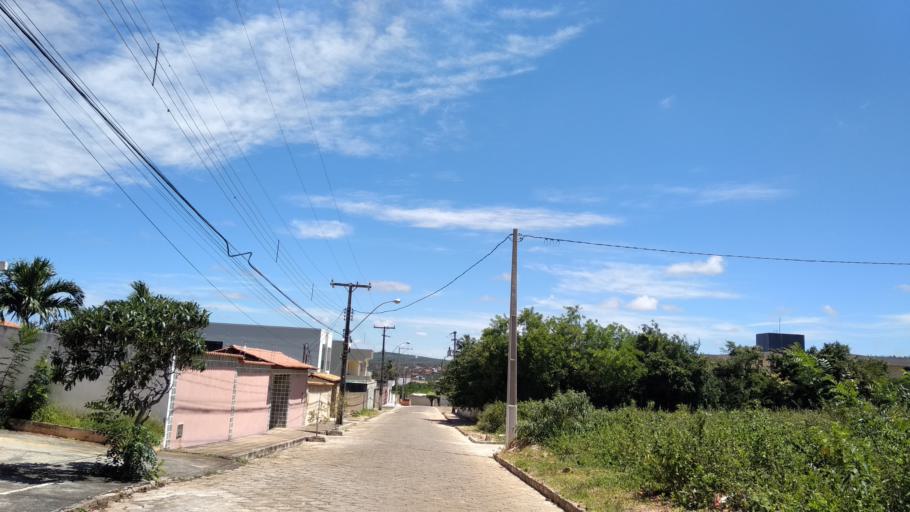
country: BR
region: Bahia
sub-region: Caetite
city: Caetite
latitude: -14.0724
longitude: -42.4823
